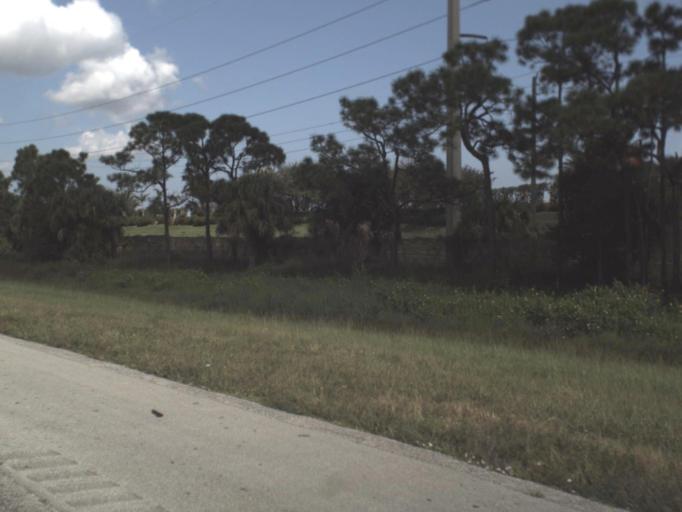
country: US
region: Florida
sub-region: Saint Lucie County
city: Port Saint Lucie
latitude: 27.2299
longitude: -80.3423
